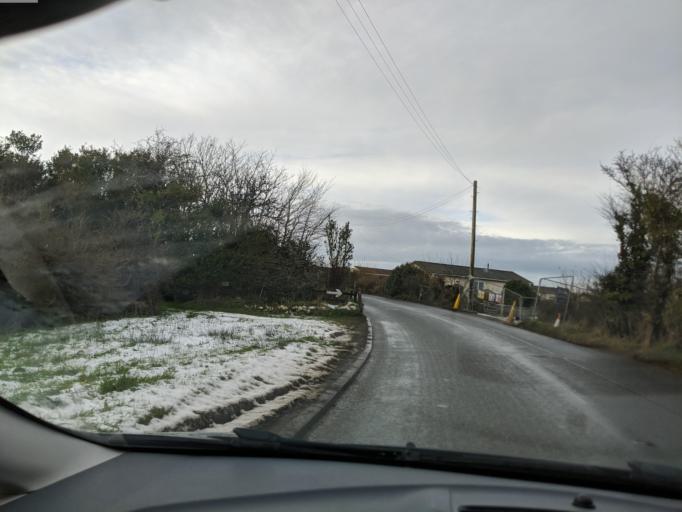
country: GB
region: England
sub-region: Cornwall
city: Jacobstow
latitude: 50.6747
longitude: -4.6099
